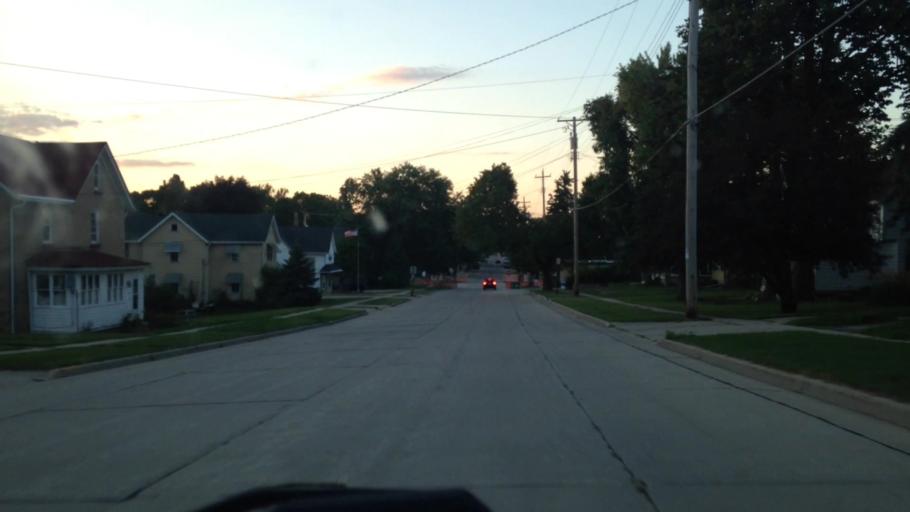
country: US
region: Wisconsin
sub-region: Dodge County
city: Mayville
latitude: 43.4924
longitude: -88.5470
